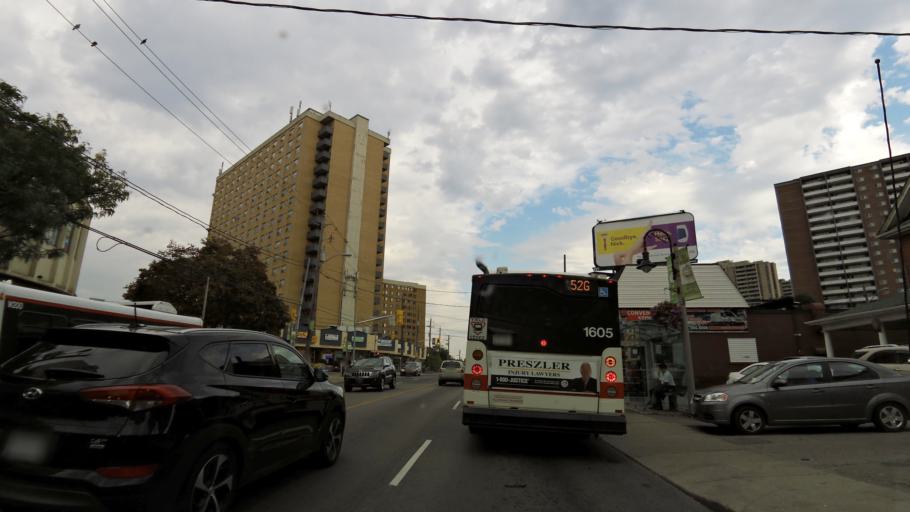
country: CA
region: Ontario
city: Etobicoke
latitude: 43.6999
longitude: -79.5172
